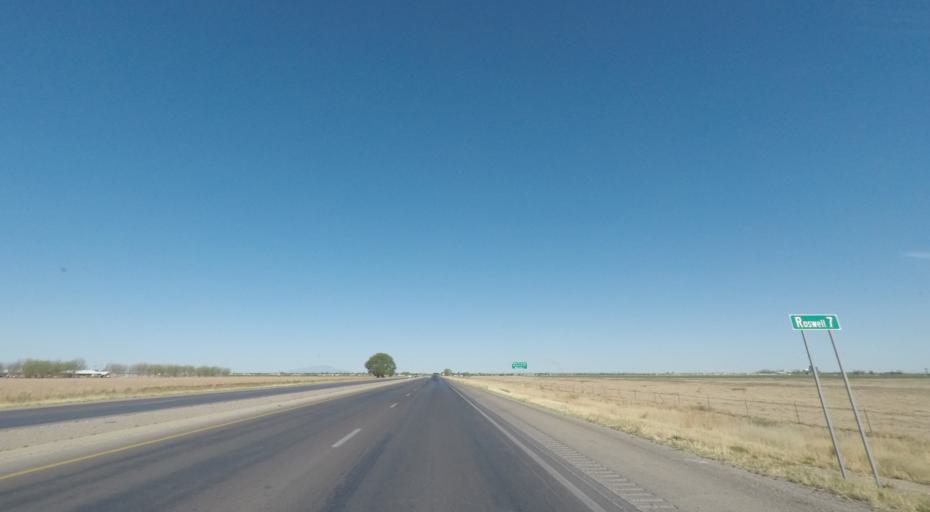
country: US
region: New Mexico
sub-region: Chaves County
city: Roswell
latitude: 33.3073
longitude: -104.4718
